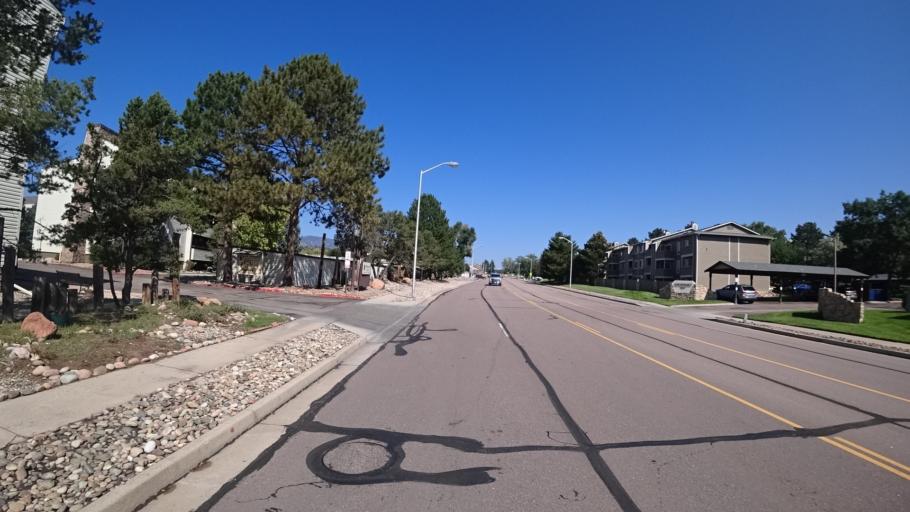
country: US
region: Colorado
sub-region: El Paso County
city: Air Force Academy
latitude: 38.9263
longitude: -104.8294
